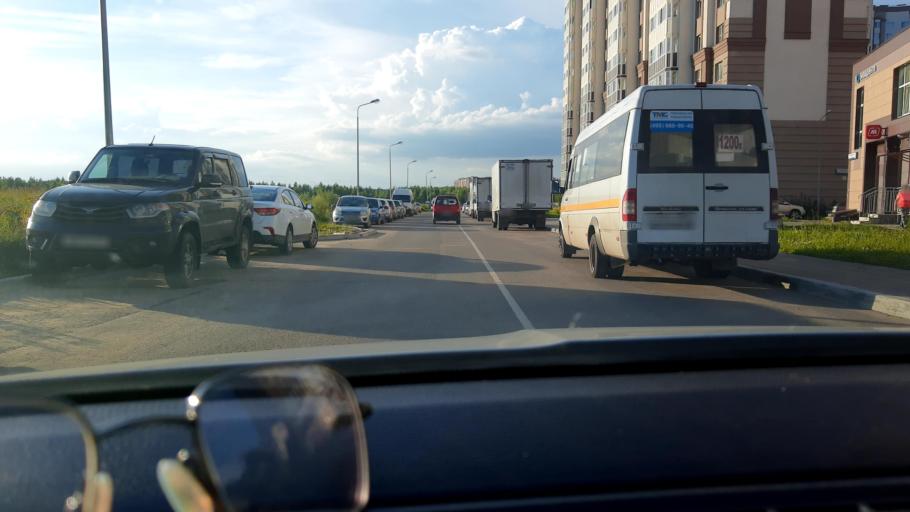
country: RU
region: Moskovskaya
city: Domodedovo
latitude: 55.4037
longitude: 37.7659
